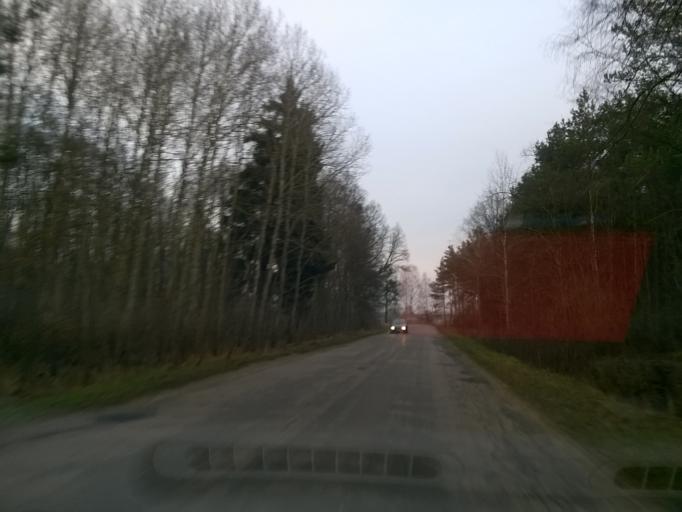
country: PL
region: Kujawsko-Pomorskie
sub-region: Powiat nakielski
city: Szubin
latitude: 53.0788
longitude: 17.7310
